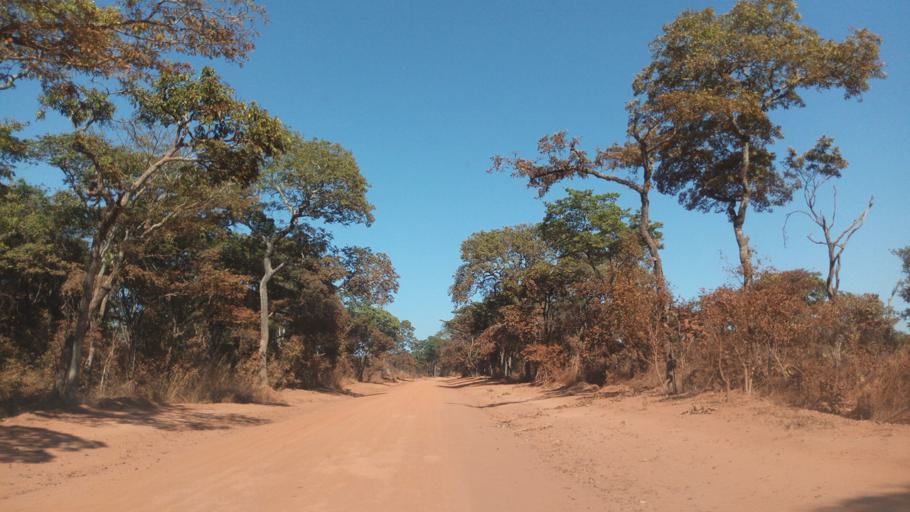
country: ZM
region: Luapula
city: Mwense
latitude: -10.7368
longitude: 28.3388
